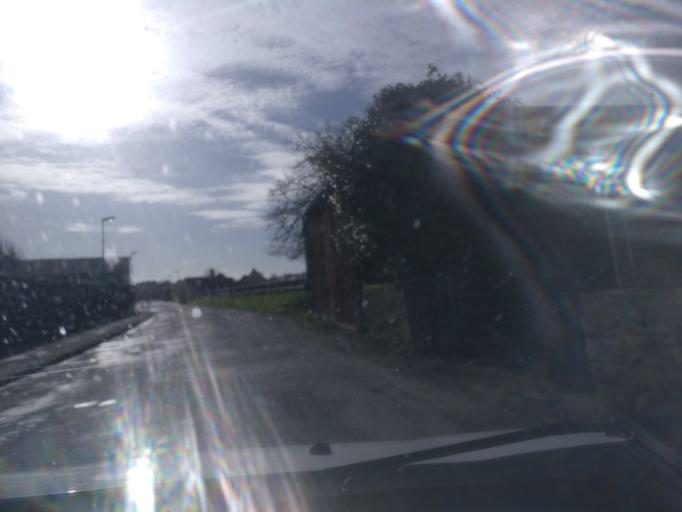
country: FR
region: Brittany
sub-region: Departement d'Ille-et-Vilaine
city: Antrain
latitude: 48.4590
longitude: -1.4854
